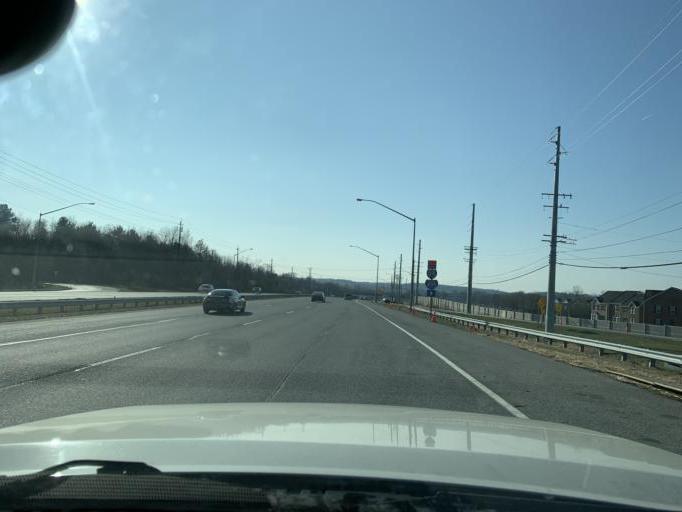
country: US
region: Maryland
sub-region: Prince George's County
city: Largo
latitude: 38.8980
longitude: -76.8328
